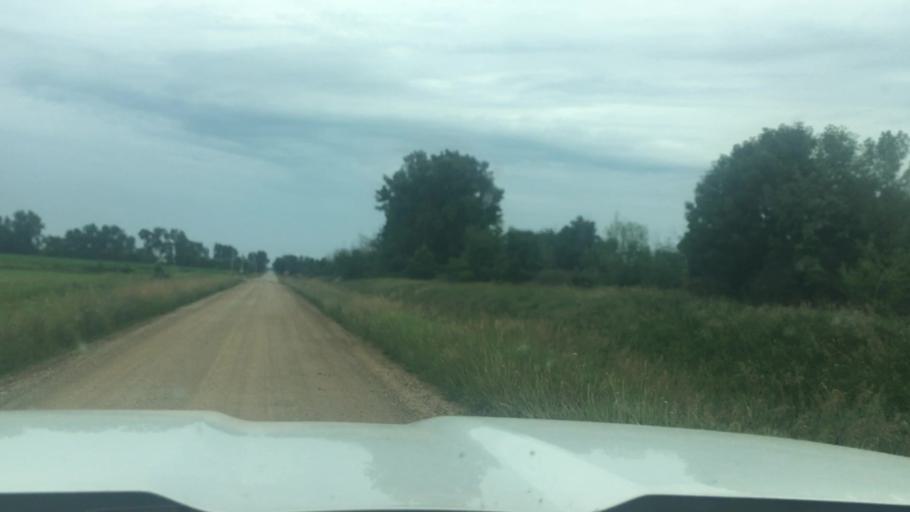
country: US
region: Michigan
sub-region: Clinton County
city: Saint Johns
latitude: 43.0619
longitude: -84.4841
